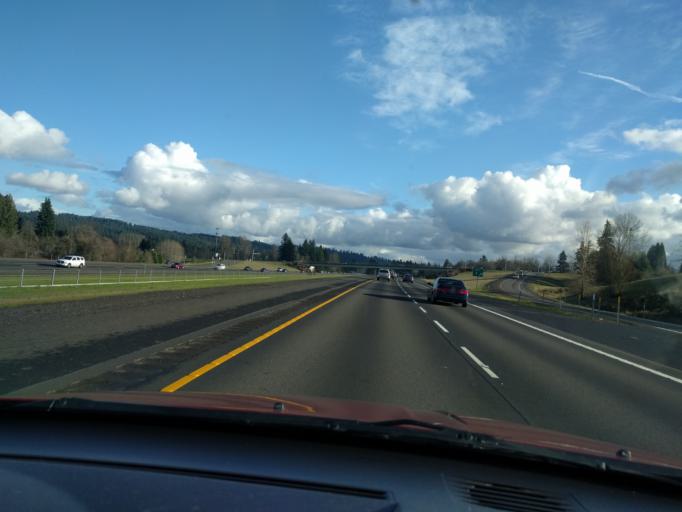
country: US
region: Oregon
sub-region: Clackamas County
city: Stafford
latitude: 45.3713
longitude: -122.7109
